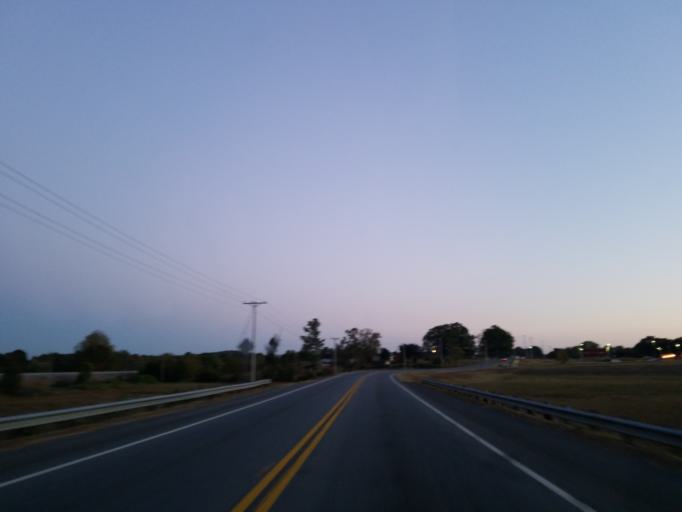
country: US
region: Georgia
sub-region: Gordon County
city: Calhoun
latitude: 34.5751
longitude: -84.9405
